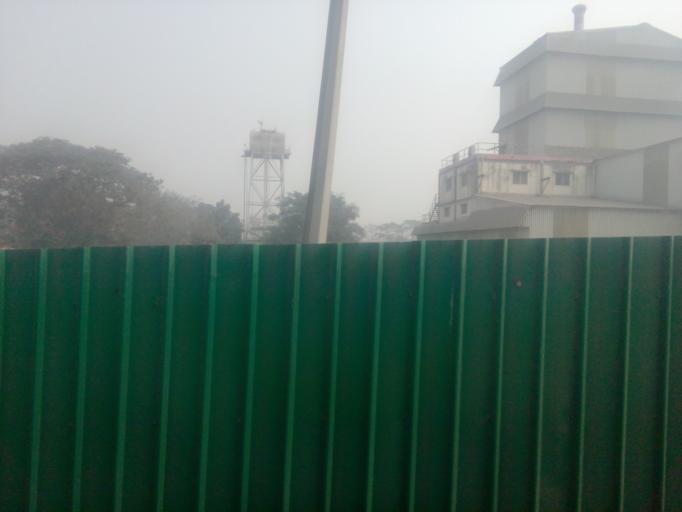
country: BD
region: Dhaka
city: Narayanganj
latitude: 23.6111
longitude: 90.6115
